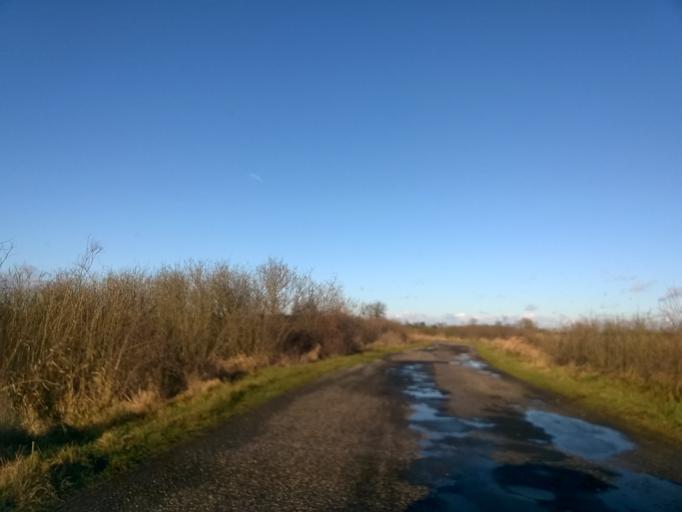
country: PL
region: Kujawsko-Pomorskie
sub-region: Powiat nakielski
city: Sadki
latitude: 53.0845
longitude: 17.4168
